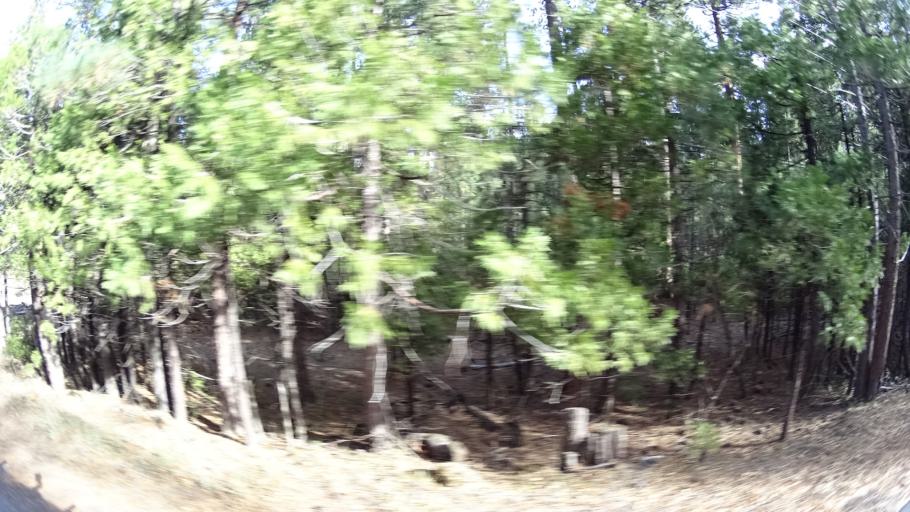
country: US
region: California
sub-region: Siskiyou County
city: Weed
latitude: 41.4106
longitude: -122.4341
